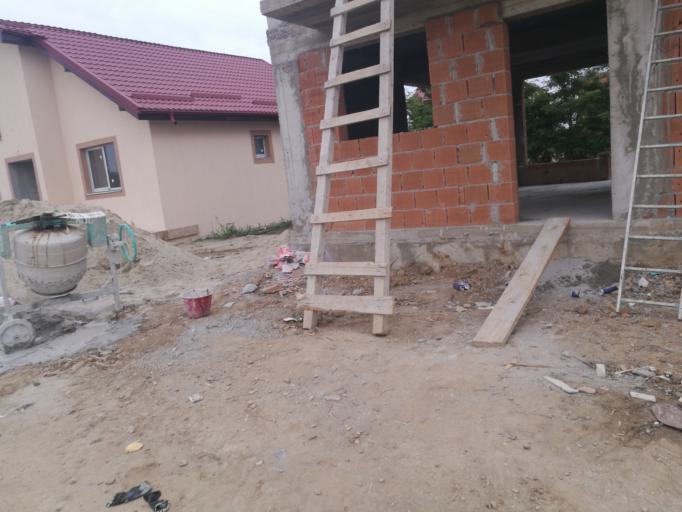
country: RO
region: Ilfov
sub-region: Comuna Vidra
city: Vidra
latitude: 44.2762
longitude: 26.1825
